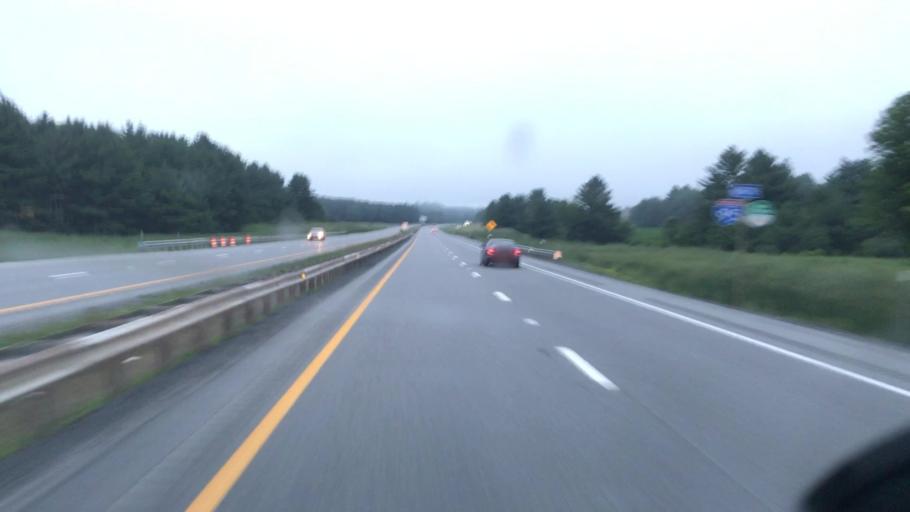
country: US
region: Maine
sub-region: Cumberland County
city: New Gloucester
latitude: 43.8858
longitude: -70.3375
